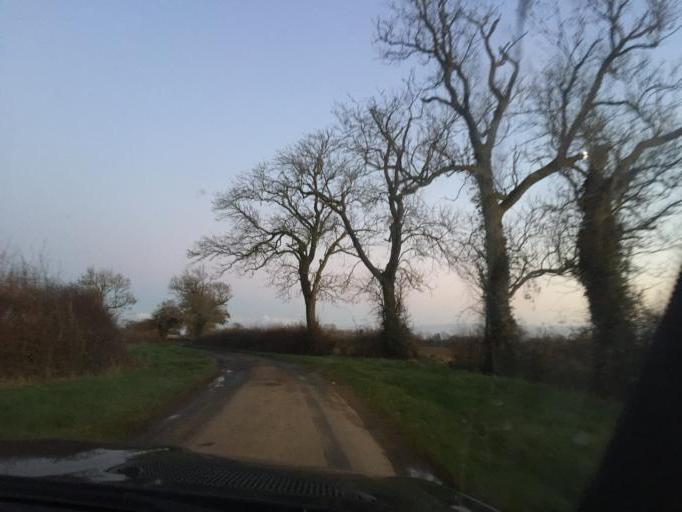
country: GB
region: England
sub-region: Northamptonshire
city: Brackley
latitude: 52.0898
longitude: -1.1033
